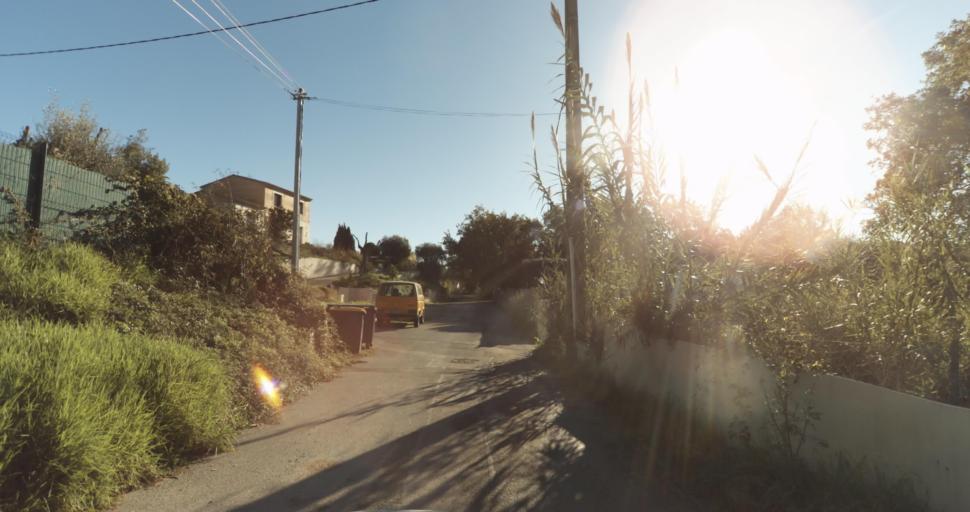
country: FR
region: Provence-Alpes-Cote d'Azur
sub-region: Departement des Alpes-Maritimes
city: Vence
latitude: 43.7233
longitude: 7.0921
